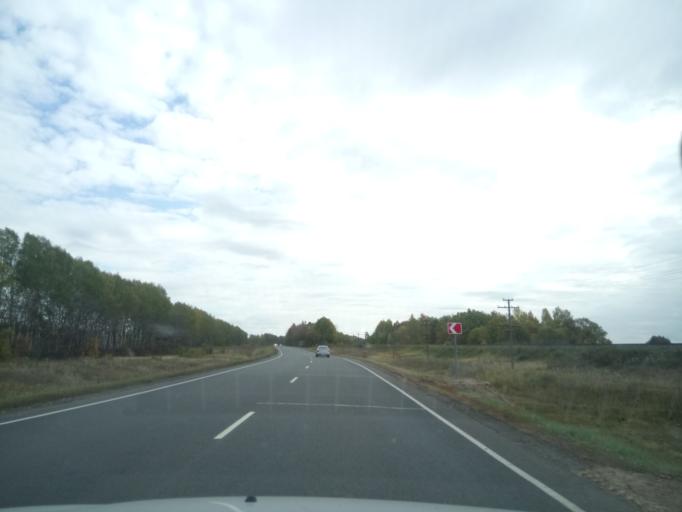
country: RU
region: Nizjnij Novgorod
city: Lukoyanov
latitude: 55.0651
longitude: 44.3502
